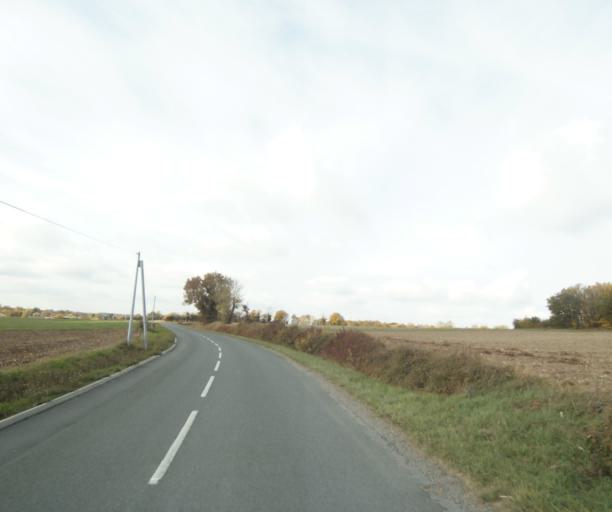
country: FR
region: Poitou-Charentes
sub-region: Departement de la Charente-Maritime
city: Saint-Georges-des-Coteaux
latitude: 45.7605
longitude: -0.6890
